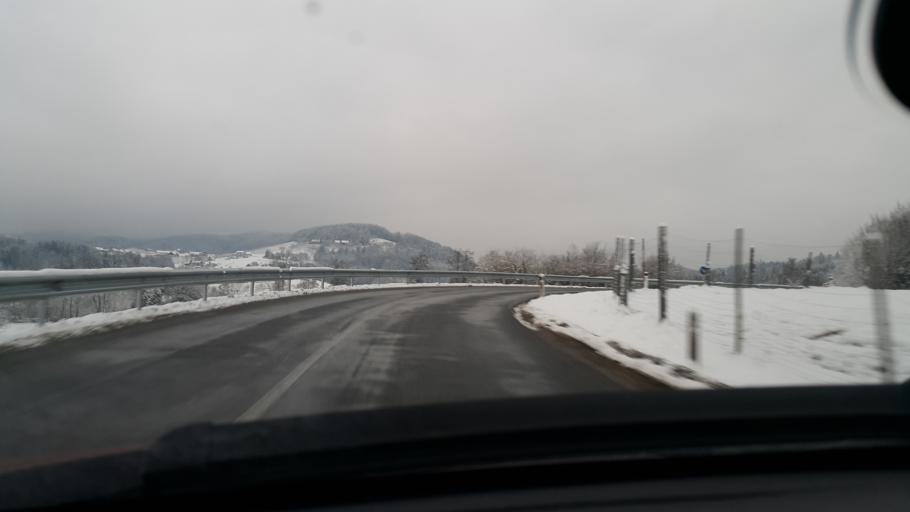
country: AT
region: Styria
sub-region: Politischer Bezirk Graz-Umgebung
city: Sankt Oswald bei Plankenwarth
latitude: 47.0746
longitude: 15.2659
